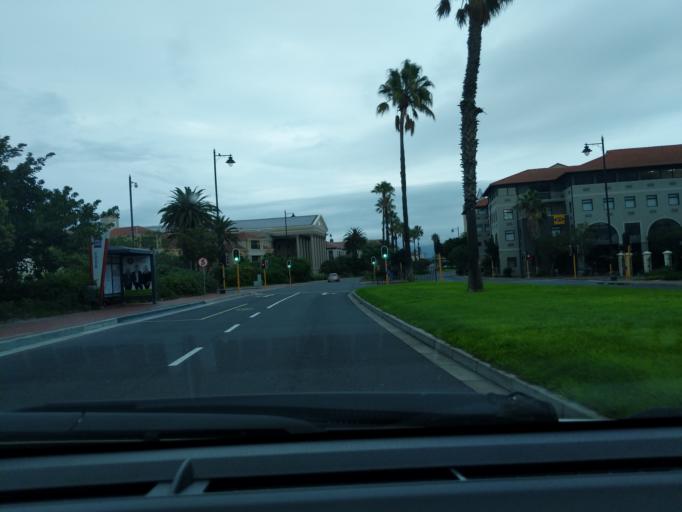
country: ZA
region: Western Cape
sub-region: City of Cape Town
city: Sunset Beach
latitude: -33.8888
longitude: 18.5196
